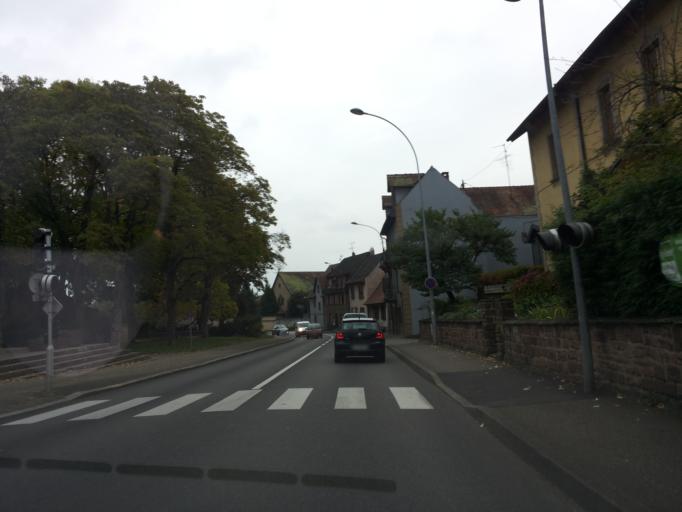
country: FR
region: Alsace
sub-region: Departement du Bas-Rhin
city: Saverne
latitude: 48.7397
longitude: 7.3618
